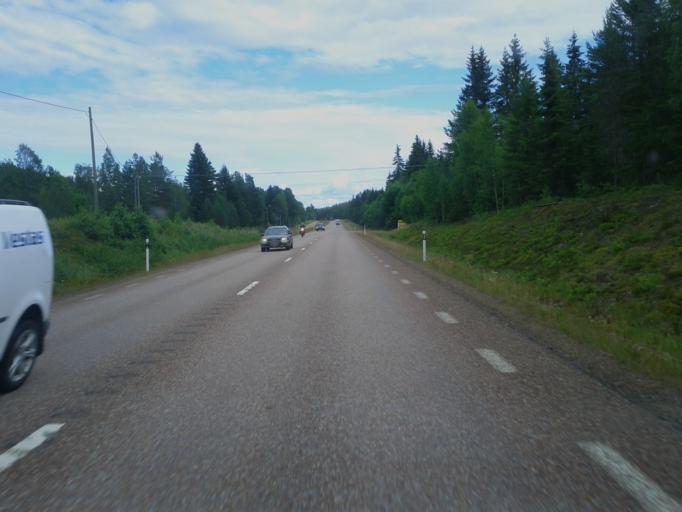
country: SE
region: Dalarna
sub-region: Faluns Kommun
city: Bjursas
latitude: 60.7430
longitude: 15.3956
